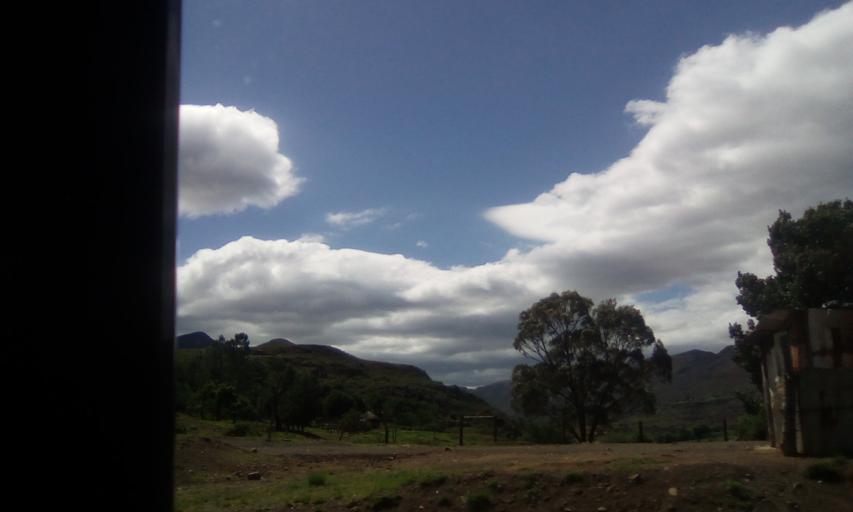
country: LS
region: Maseru
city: Nako
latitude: -29.6612
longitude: 27.8065
